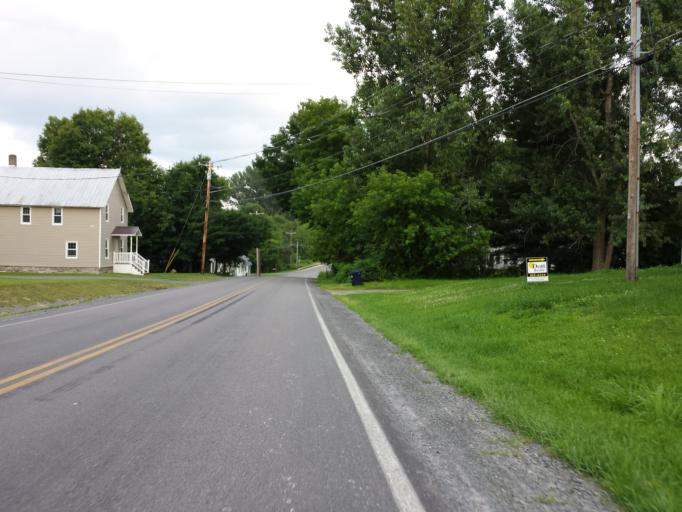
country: US
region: New York
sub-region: St. Lawrence County
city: Potsdam
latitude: 44.7148
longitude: -74.9023
